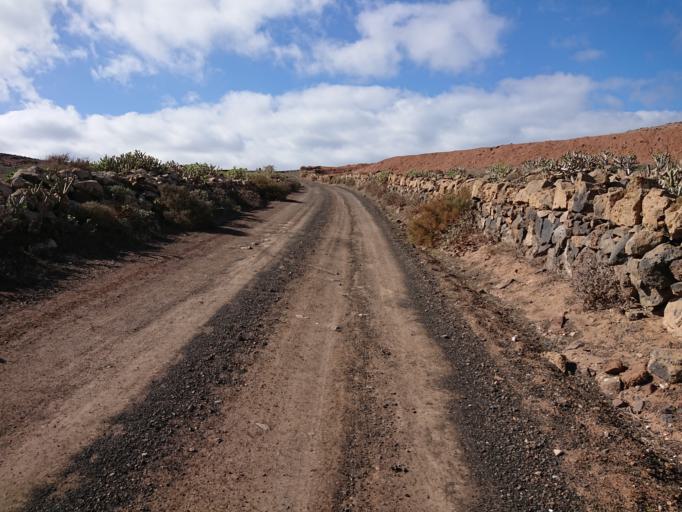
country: ES
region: Canary Islands
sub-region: Provincia de Las Palmas
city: Haria
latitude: 29.1456
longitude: -13.5179
